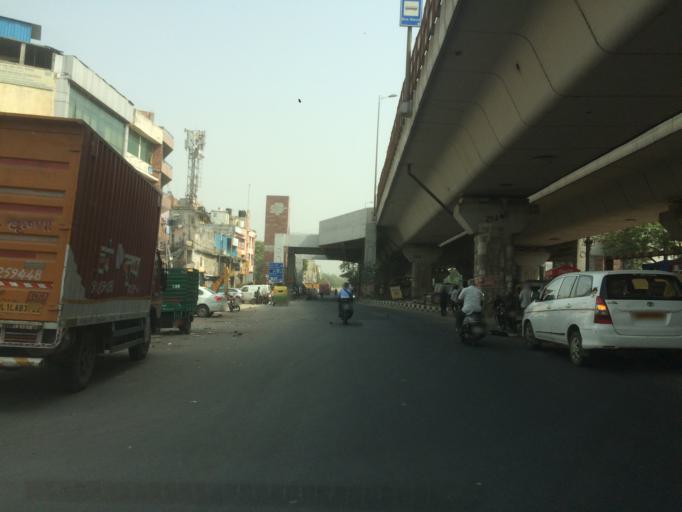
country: IN
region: NCT
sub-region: Central Delhi
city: Karol Bagh
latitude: 28.6249
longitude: 77.1346
